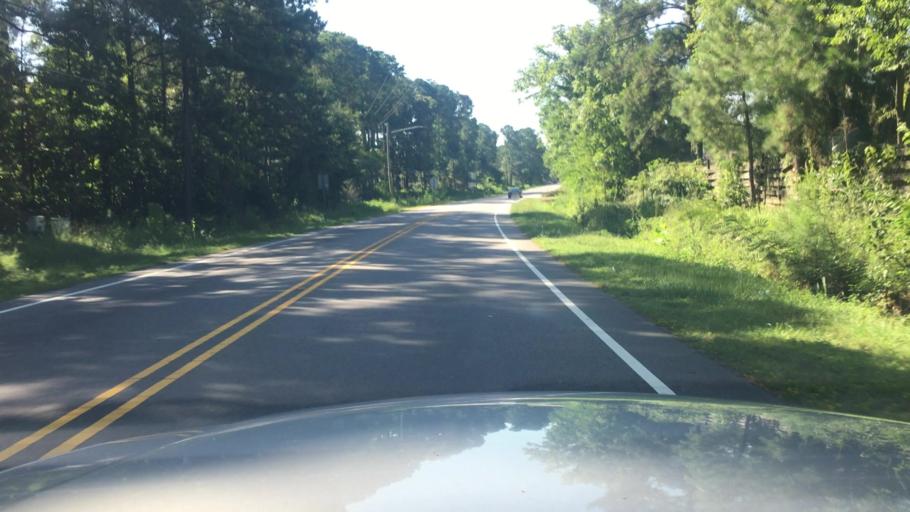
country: US
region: North Carolina
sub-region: Cumberland County
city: Fayetteville
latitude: 35.1103
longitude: -78.9031
